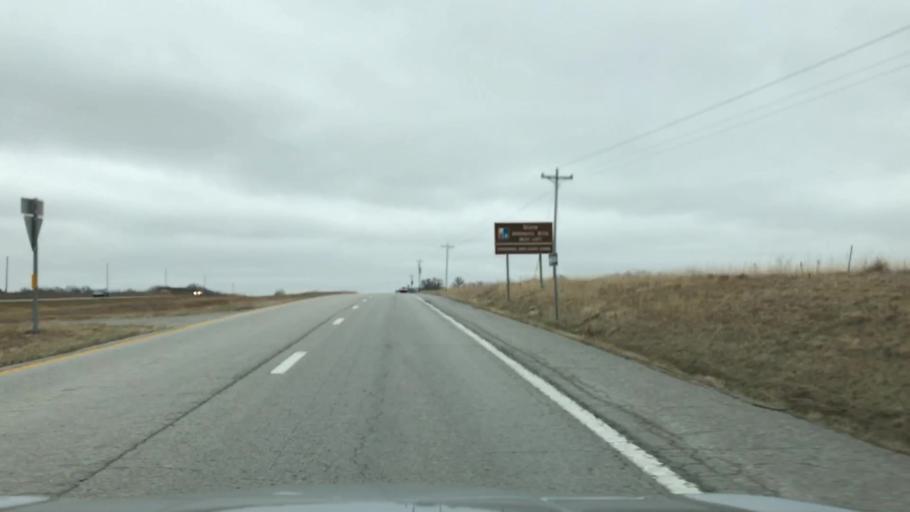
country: US
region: Missouri
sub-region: Linn County
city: Linneus
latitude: 39.7782
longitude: -93.1839
